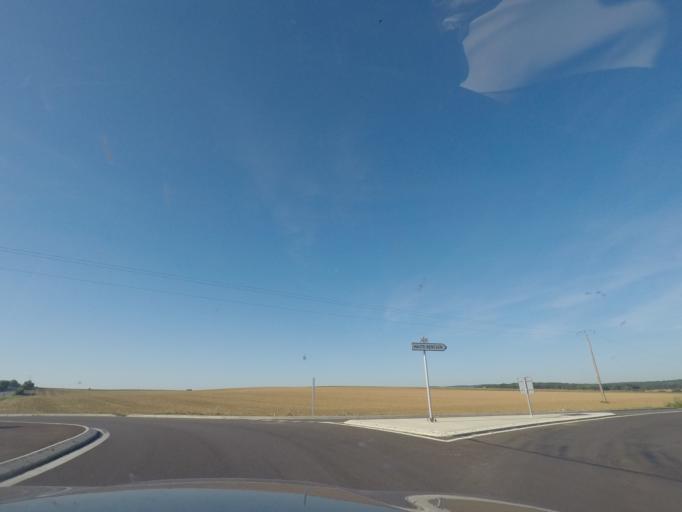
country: LU
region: Luxembourg
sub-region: Canton d'Esch-sur-Alzette
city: Frisange
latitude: 49.4869
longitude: 6.1911
